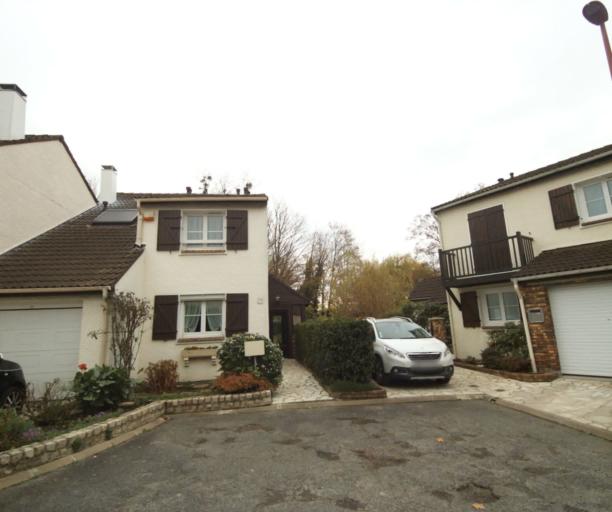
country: FR
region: Ile-de-France
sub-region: Departement du Val-d'Oise
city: Gonesse
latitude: 48.9812
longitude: 2.4364
